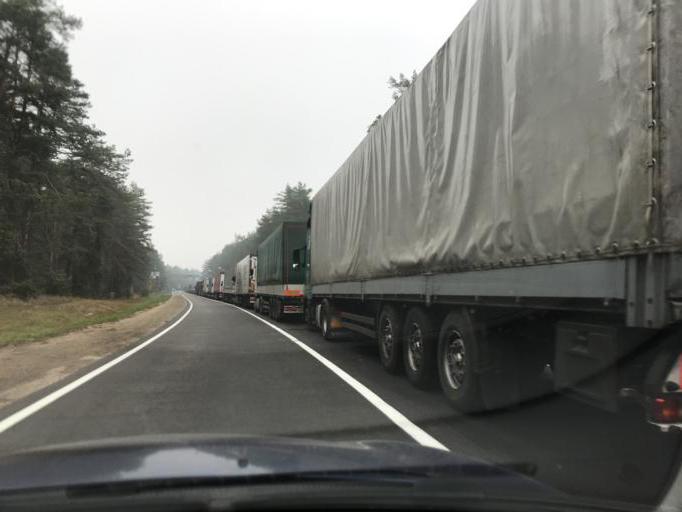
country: LT
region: Alytaus apskritis
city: Druskininkai
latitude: 53.9353
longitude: 23.9509
